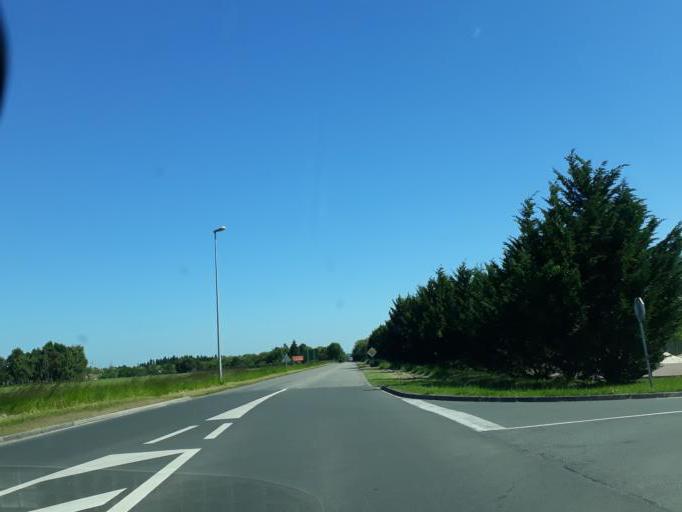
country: FR
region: Centre
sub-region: Departement du Loiret
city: Nevoy
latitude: 47.7128
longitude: 2.5887
